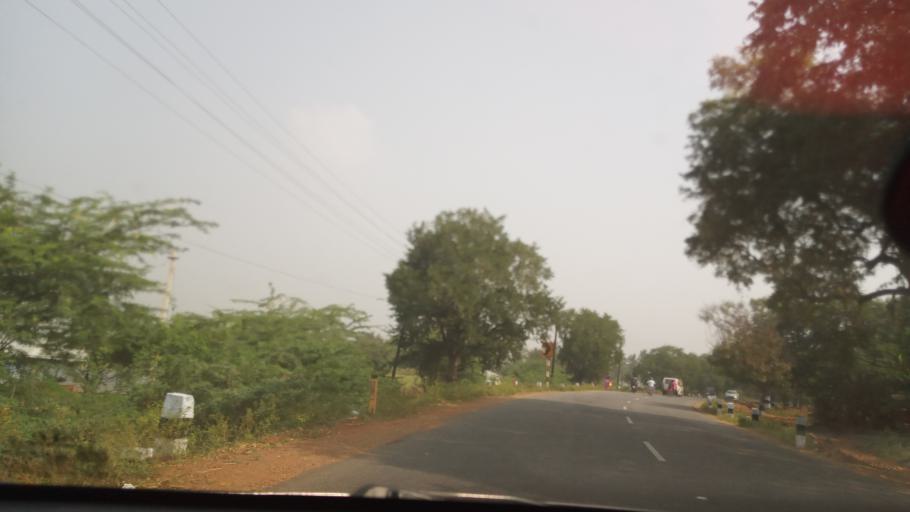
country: IN
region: Tamil Nadu
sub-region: Erode
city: Sathyamangalam
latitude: 11.4385
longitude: 77.2050
